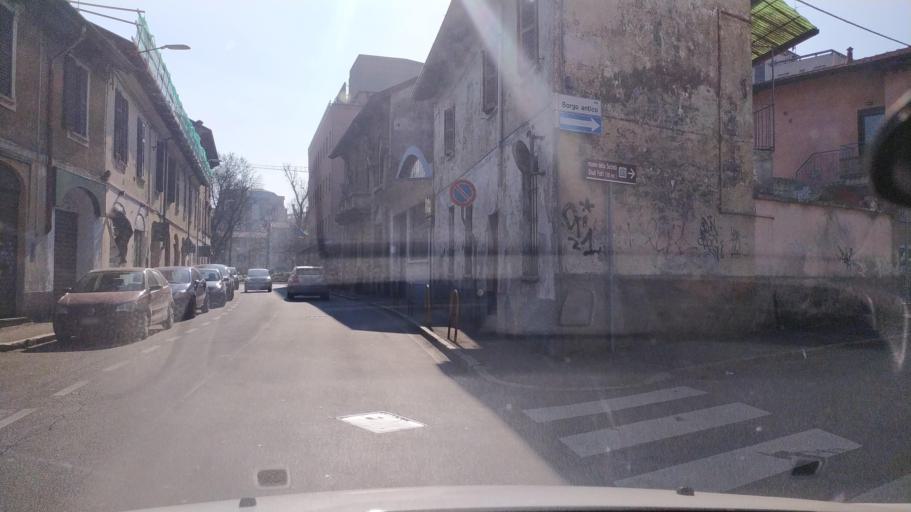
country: IT
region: Lombardy
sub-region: Provincia di Varese
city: Gallarate
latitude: 45.6635
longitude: 8.7935
